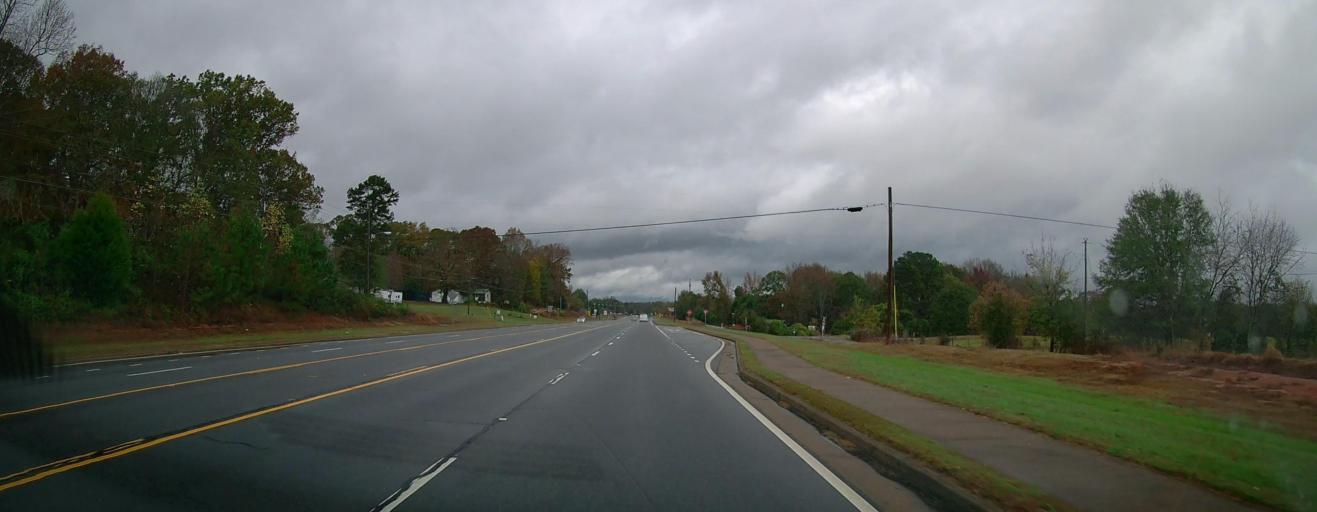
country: US
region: Georgia
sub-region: Jackson County
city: Nicholson
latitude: 34.1034
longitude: -83.4333
